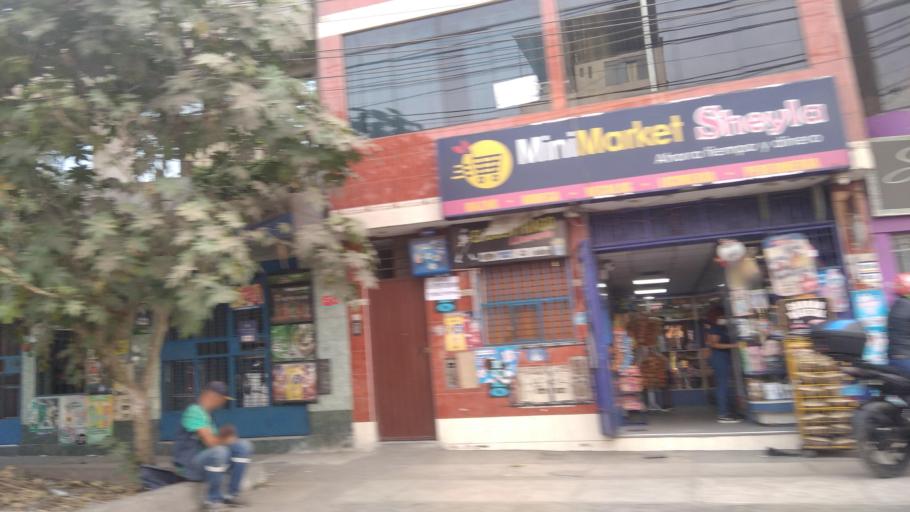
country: PE
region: Lima
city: Lima
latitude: -12.0145
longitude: -76.9971
